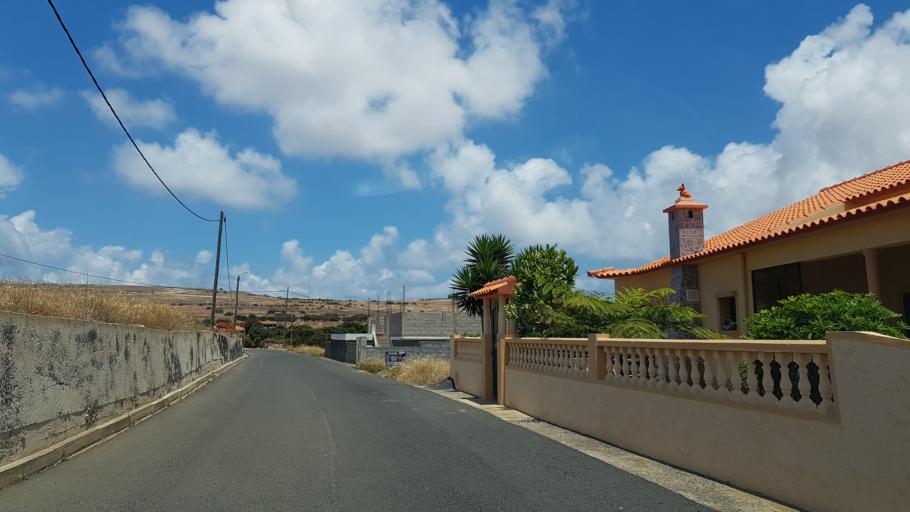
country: PT
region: Madeira
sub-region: Porto Santo
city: Vila de Porto Santo
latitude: 33.0585
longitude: -16.3599
